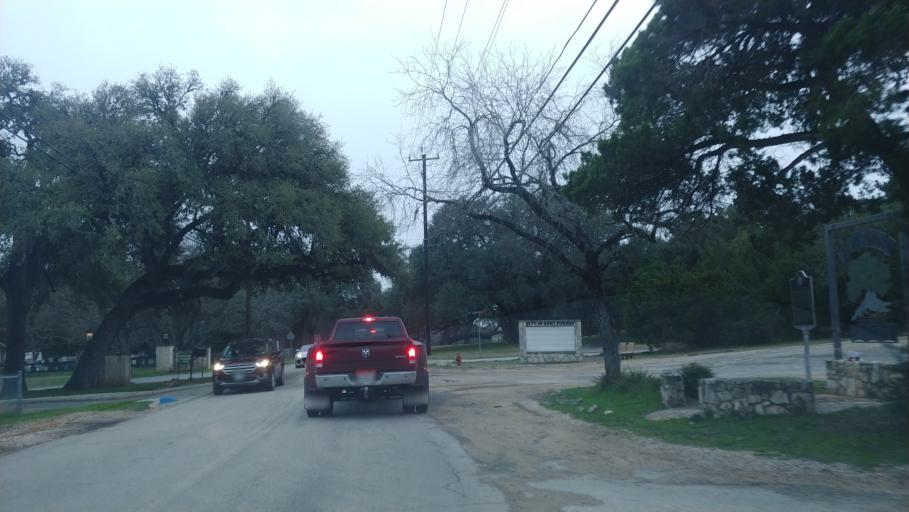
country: US
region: Texas
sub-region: Bexar County
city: Helotes
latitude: 29.6146
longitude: -98.6850
